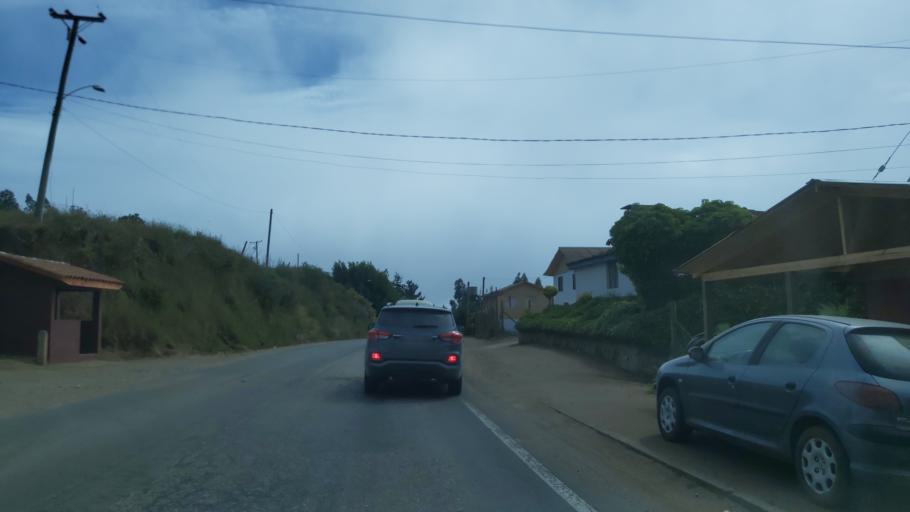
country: CL
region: Maule
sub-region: Provincia de Cauquenes
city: Cauquenes
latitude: -35.8702
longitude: -72.6561
